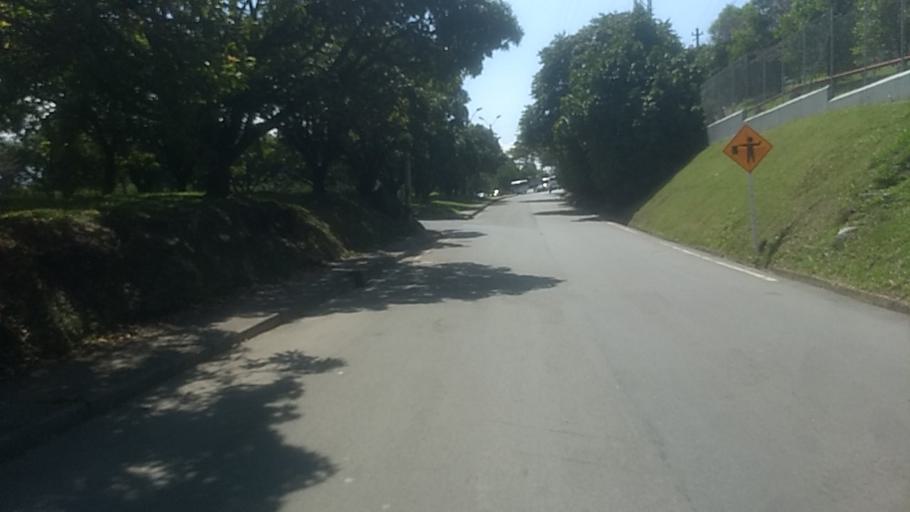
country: CO
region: Antioquia
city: Bello
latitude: 6.3036
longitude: -75.5629
